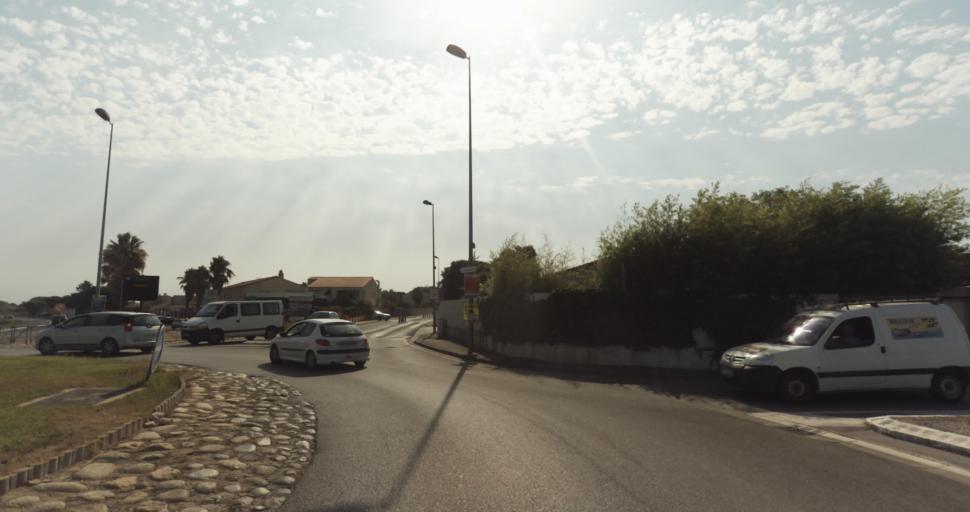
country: FR
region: Languedoc-Roussillon
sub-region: Departement des Pyrenees-Orientales
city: Latour-Bas-Elne
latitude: 42.6071
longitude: 2.9967
